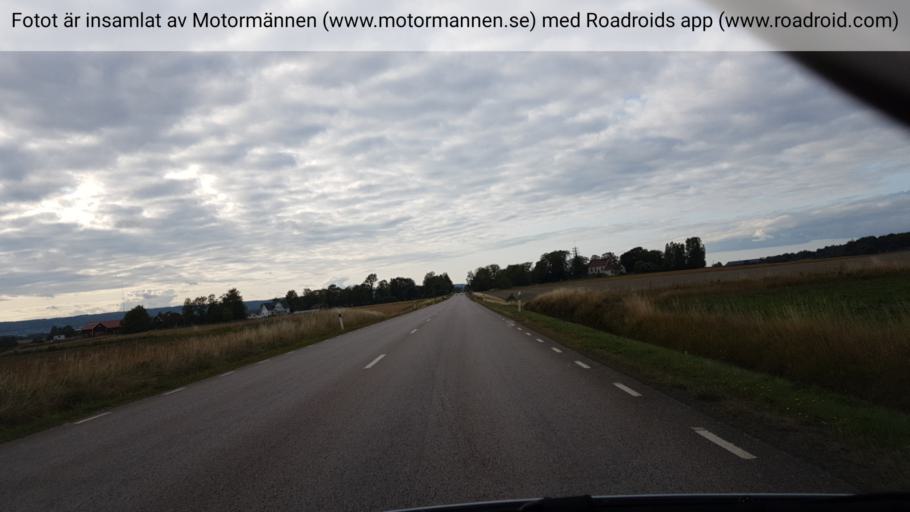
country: SE
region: Vaestra Goetaland
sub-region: Skovde Kommun
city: Skoevde
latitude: 58.3855
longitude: 13.9428
